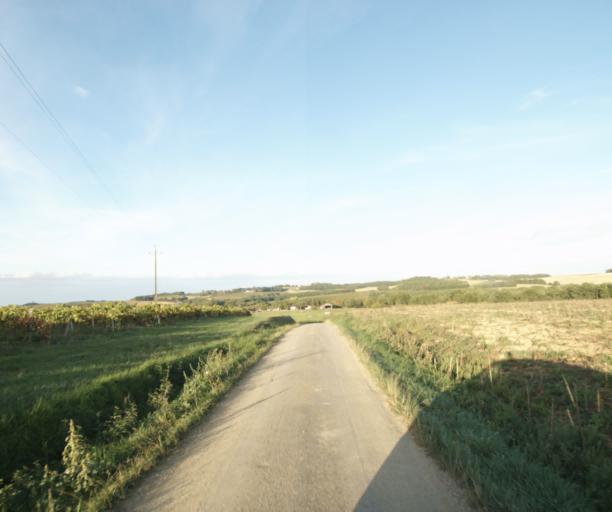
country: FR
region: Midi-Pyrenees
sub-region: Departement du Gers
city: Gondrin
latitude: 43.8593
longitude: 0.2998
